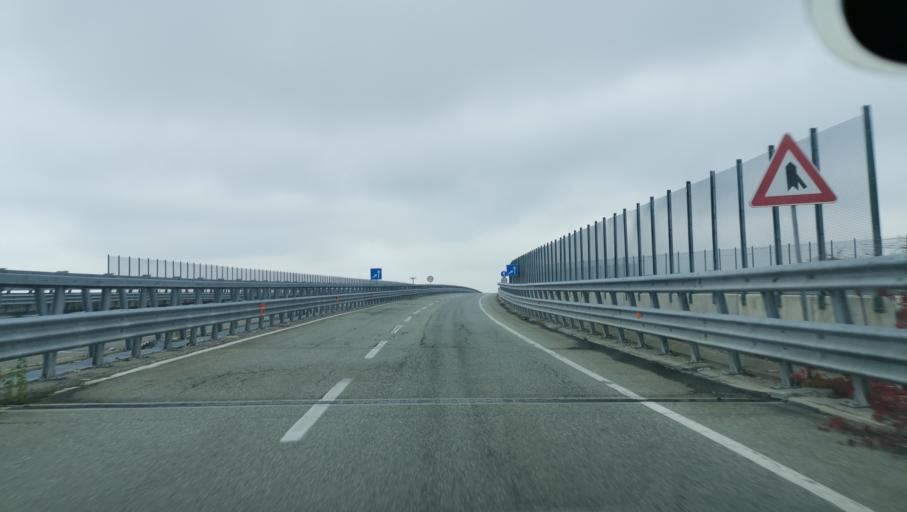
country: IT
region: Piedmont
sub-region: Provincia di Torino
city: Brandizzo
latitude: 45.1662
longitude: 7.8172
